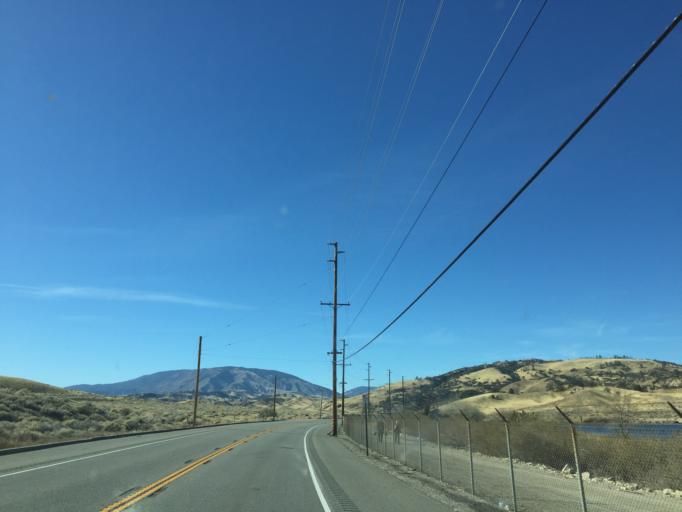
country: US
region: California
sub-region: Kern County
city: Lebec
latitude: 34.7701
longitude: -118.7545
